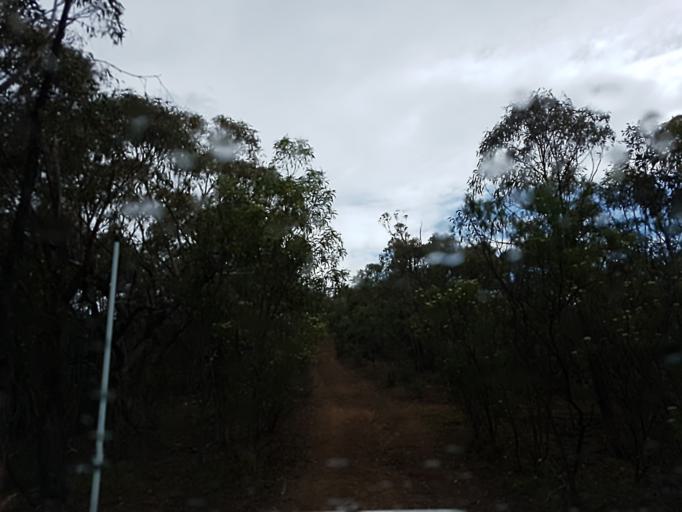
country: AU
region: New South Wales
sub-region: Snowy River
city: Jindabyne
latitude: -36.9064
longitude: 148.3407
